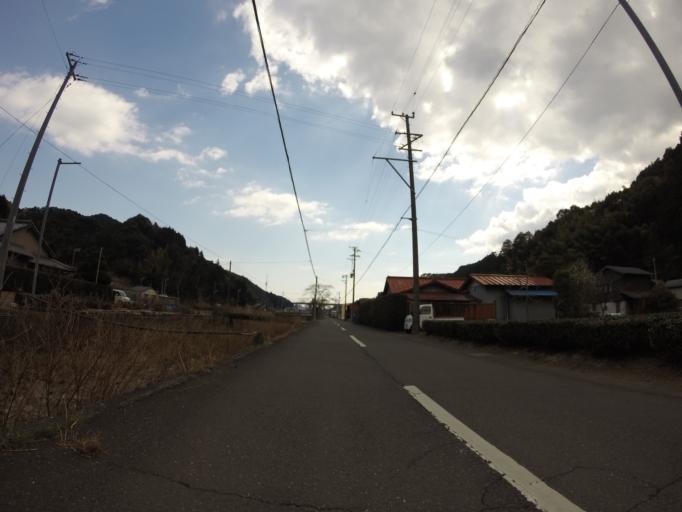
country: JP
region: Shizuoka
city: Shizuoka-shi
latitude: 35.0295
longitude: 138.3400
